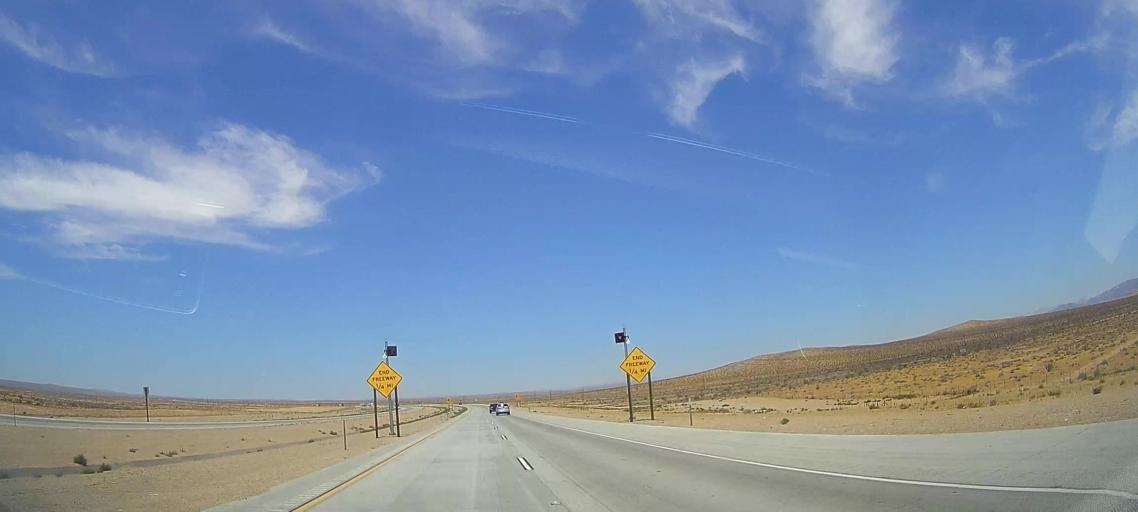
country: US
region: California
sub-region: San Bernardino County
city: Lenwood
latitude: 34.9186
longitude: -117.2450
